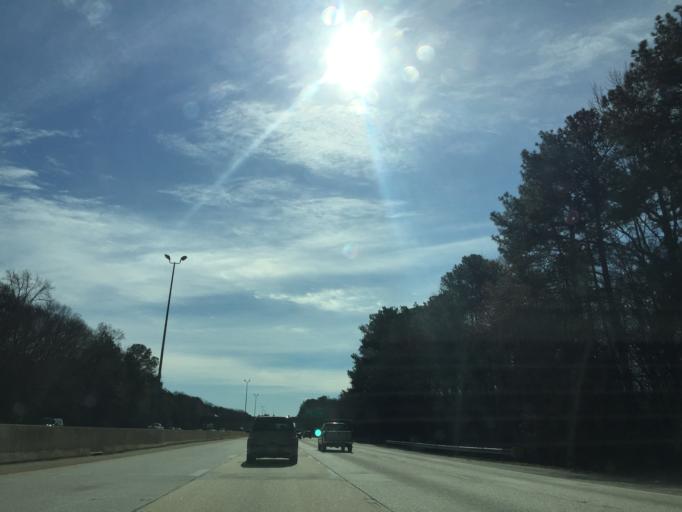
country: US
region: Virginia
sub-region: City of Hampton
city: Hampton
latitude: 37.0610
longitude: -76.4204
